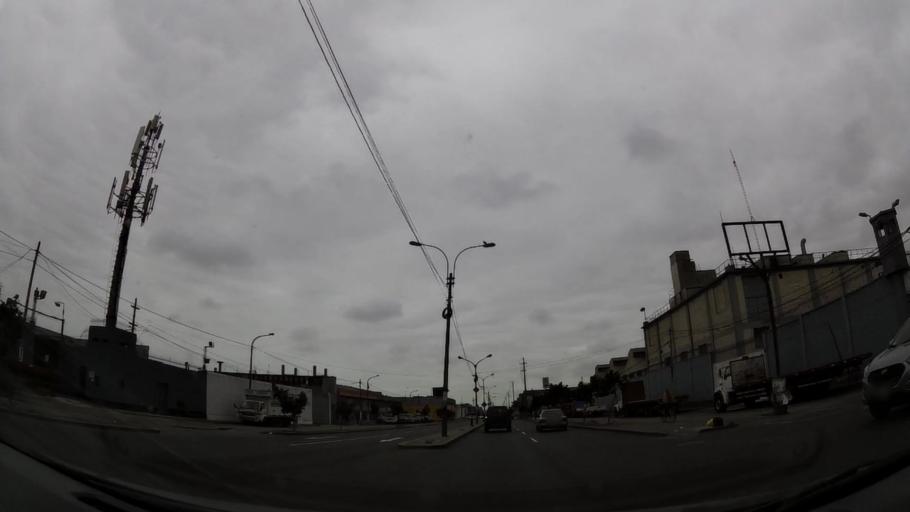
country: PE
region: Lima
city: Lima
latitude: -12.0446
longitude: -77.0562
